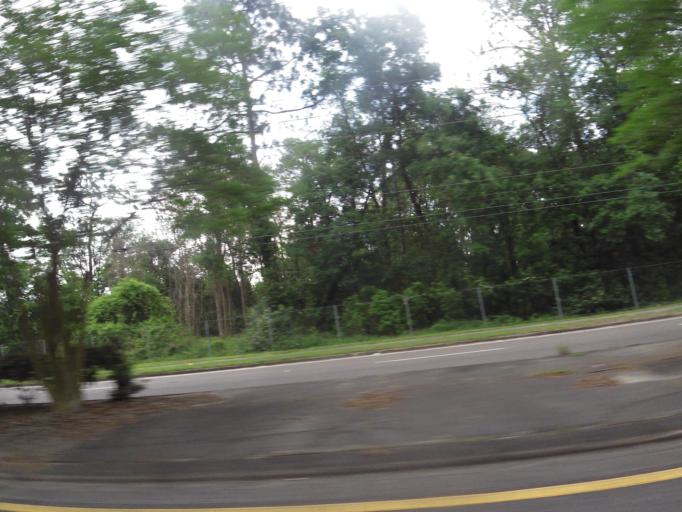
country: US
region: Florida
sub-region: Clay County
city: Bellair-Meadowbrook Terrace
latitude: 30.2876
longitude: -81.7670
